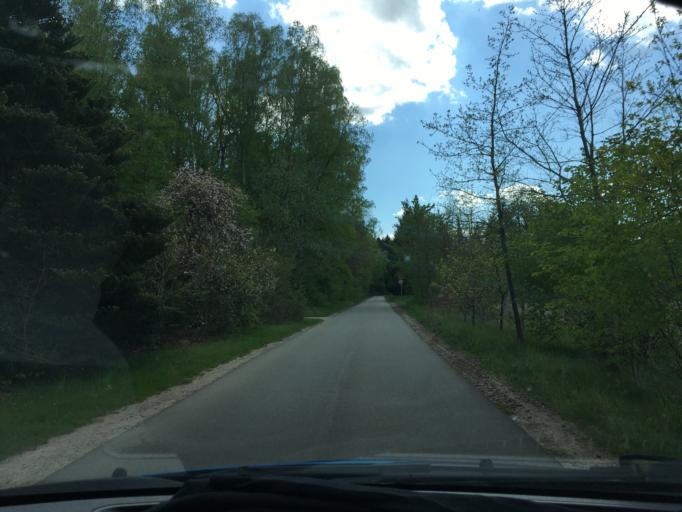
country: DE
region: Lower Saxony
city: Nahrendorf
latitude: 53.1444
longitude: 10.8088
